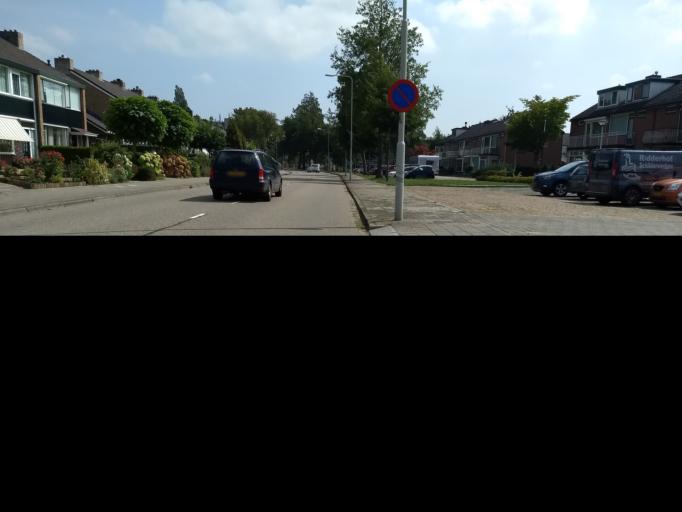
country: NL
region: South Holland
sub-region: Gemeente Papendrecht
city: Papendrecht
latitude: 51.8293
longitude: 4.6796
